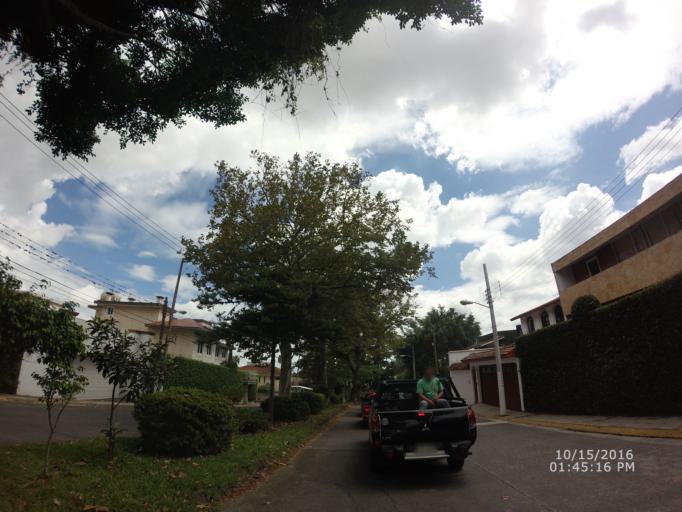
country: MX
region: Veracruz
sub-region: Xalapa
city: Lomas Verdes
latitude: 19.5256
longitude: -96.8842
